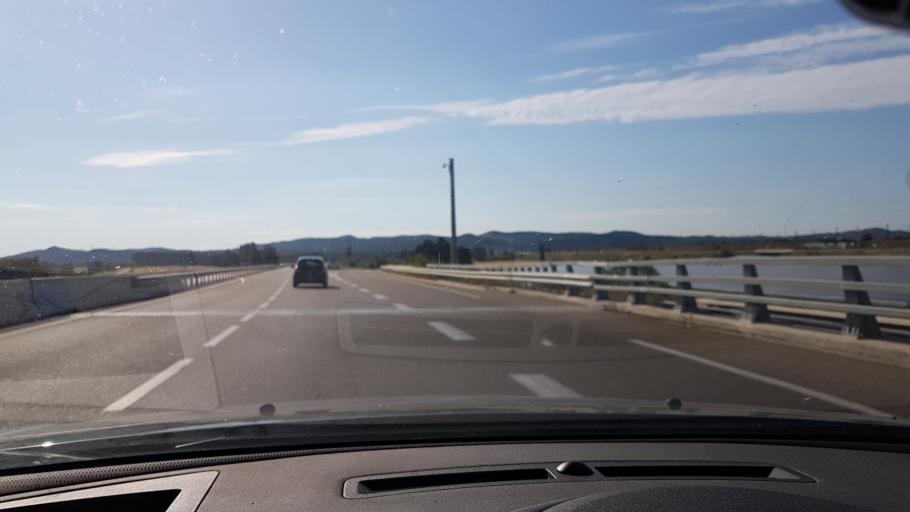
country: FR
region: Provence-Alpes-Cote d'Azur
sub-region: Departement des Bouches-du-Rhone
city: Rognonas
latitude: 43.9213
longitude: 4.7812
